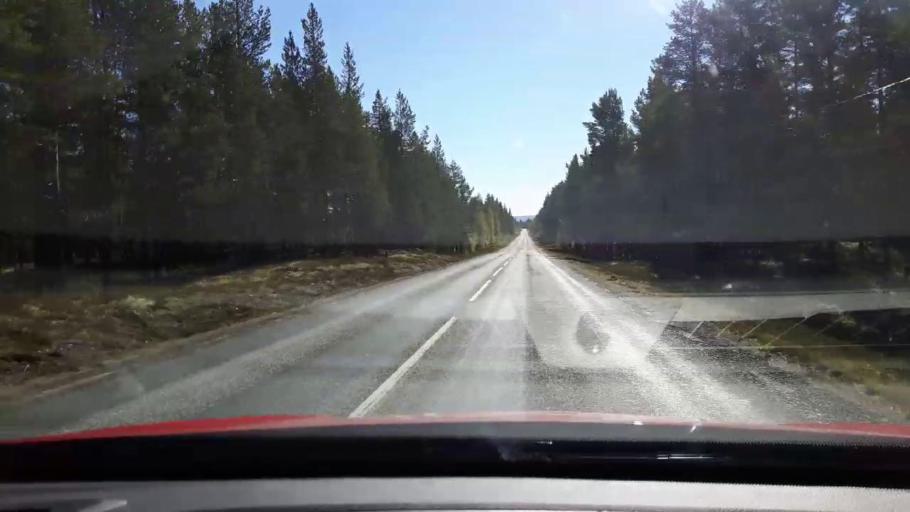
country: SE
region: Jaemtland
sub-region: Harjedalens Kommun
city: Sveg
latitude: 62.3739
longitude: 13.9790
